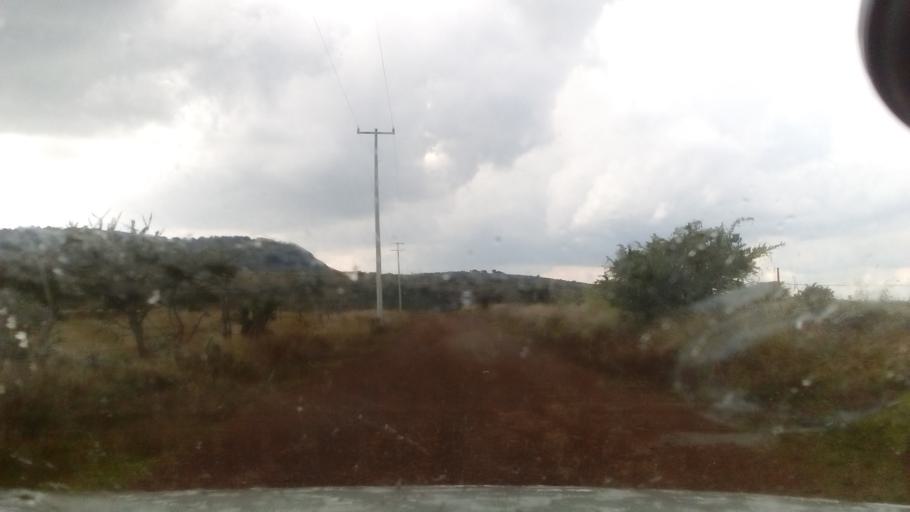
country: MX
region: Guanajuato
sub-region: Silao de la Victoria
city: San Francisco (Banos de Agua Caliente)
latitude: 21.1597
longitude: -101.4284
